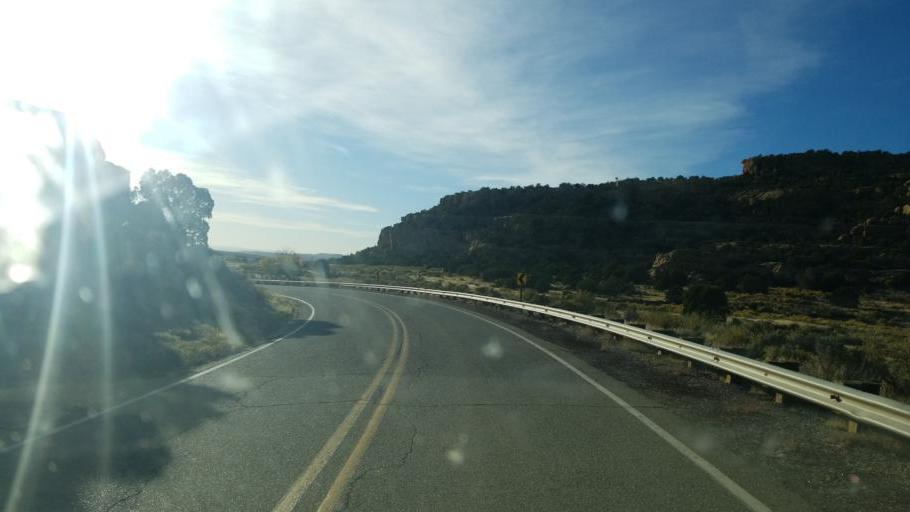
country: US
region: New Mexico
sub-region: San Juan County
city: Bloomfield
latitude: 36.7393
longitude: -107.7325
